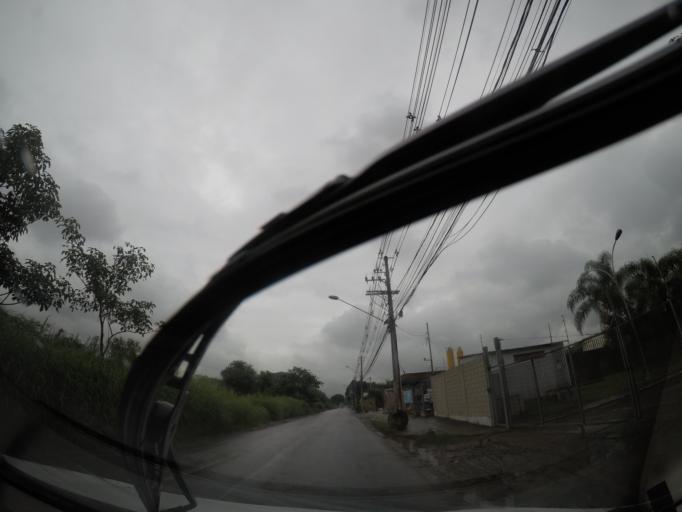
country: BR
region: Sao Paulo
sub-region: Guarulhos
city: Guarulhos
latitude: -23.4747
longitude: -46.4577
